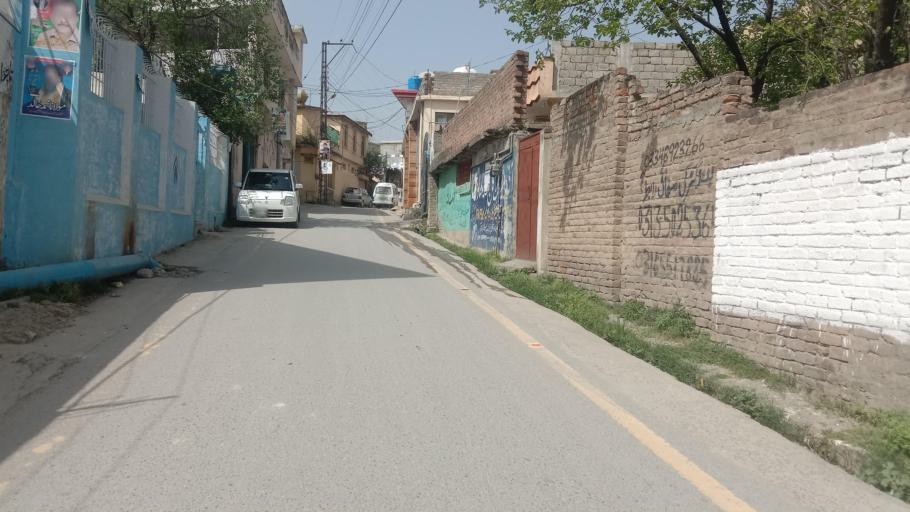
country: PK
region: Khyber Pakhtunkhwa
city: Abbottabad
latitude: 34.1485
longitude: 73.2020
